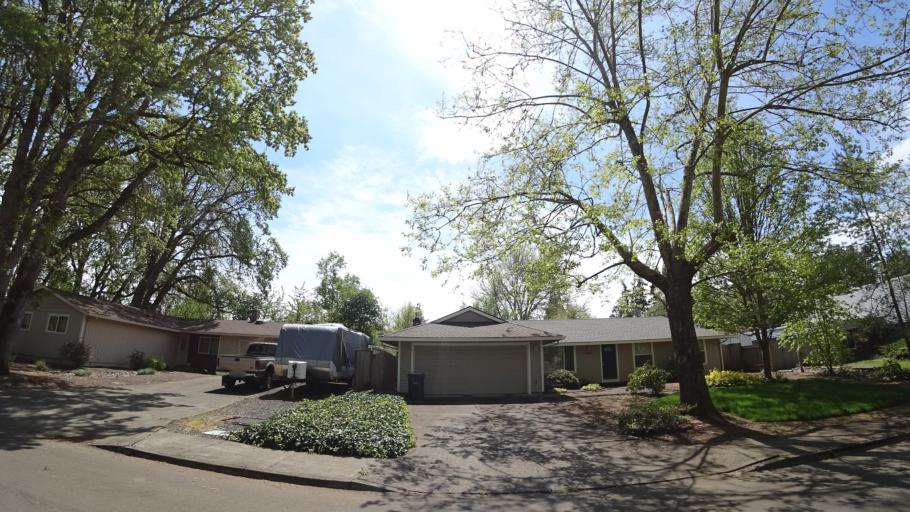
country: US
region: Oregon
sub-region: Washington County
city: Aloha
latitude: 45.4768
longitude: -122.8844
